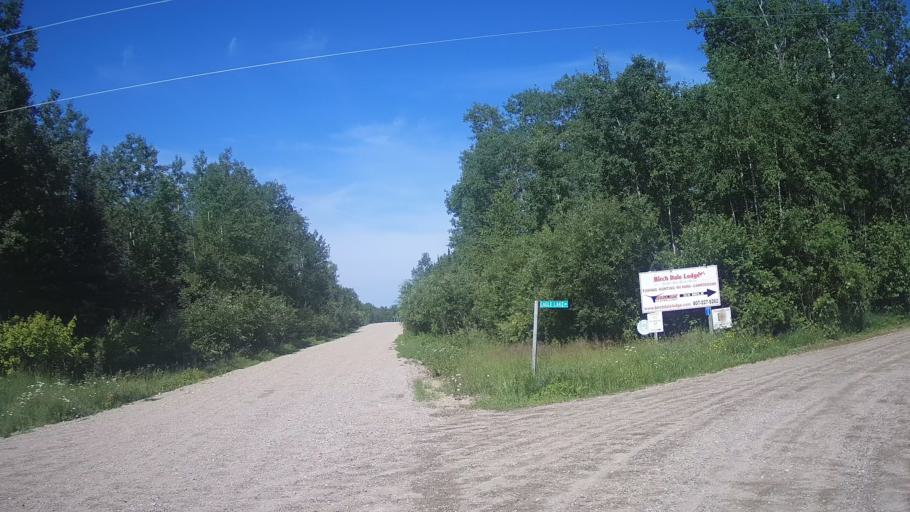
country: CA
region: Ontario
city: Dryden
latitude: 49.8152
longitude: -93.3281
